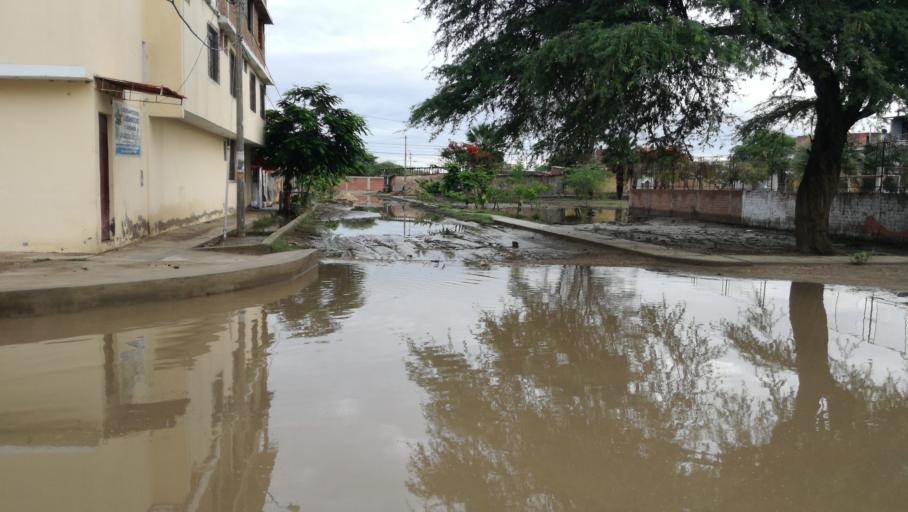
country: PE
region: Piura
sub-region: Provincia de Piura
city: Piura
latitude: -5.1695
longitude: -80.6312
